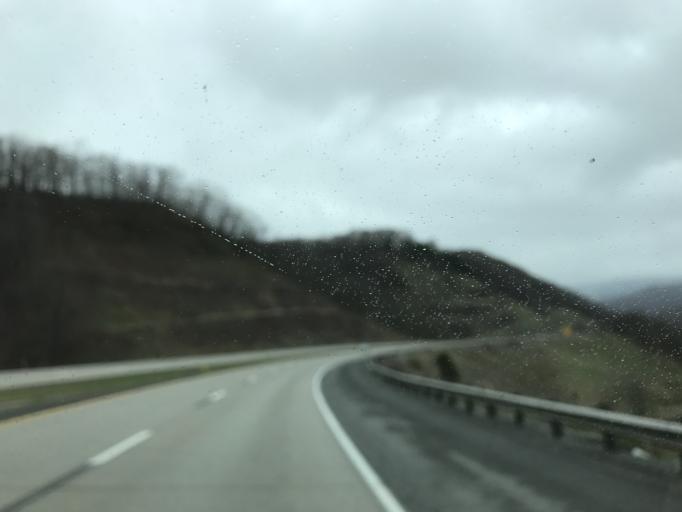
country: US
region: West Virginia
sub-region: Summers County
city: Hinton
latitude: 37.7823
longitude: -80.9670
